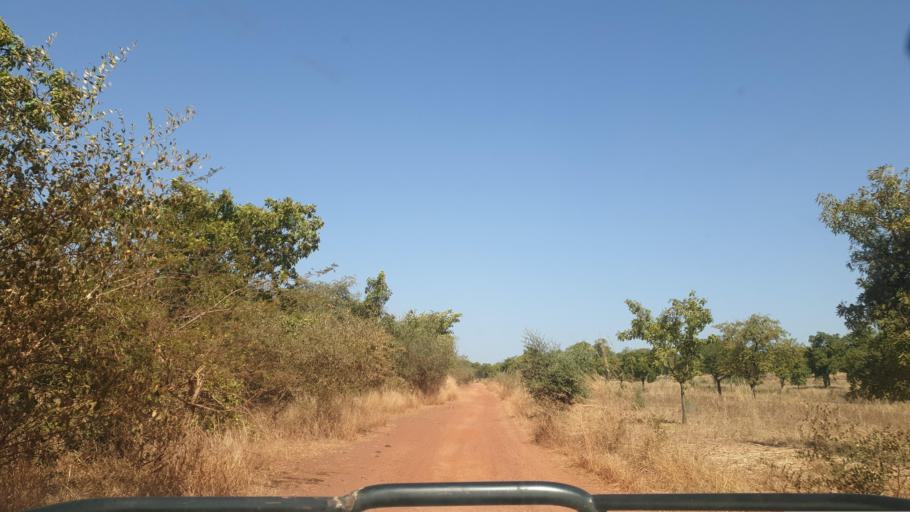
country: ML
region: Koulikoro
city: Dioila
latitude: 11.9066
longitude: -6.9831
